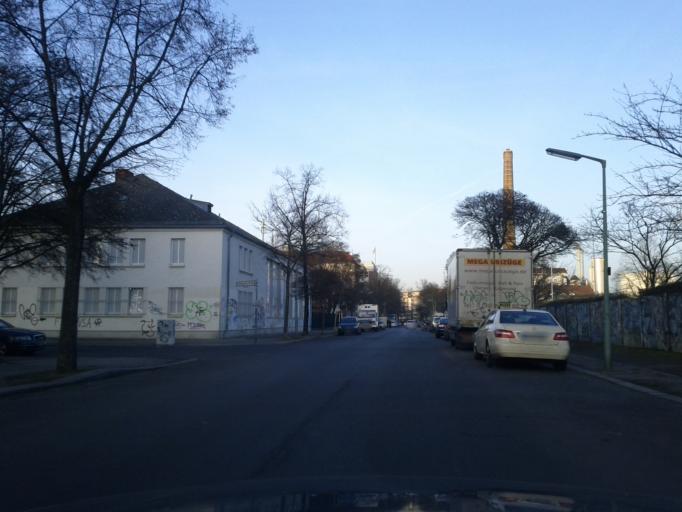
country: DE
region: Berlin
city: Treptow Bezirk
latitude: 52.4772
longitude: 13.4507
